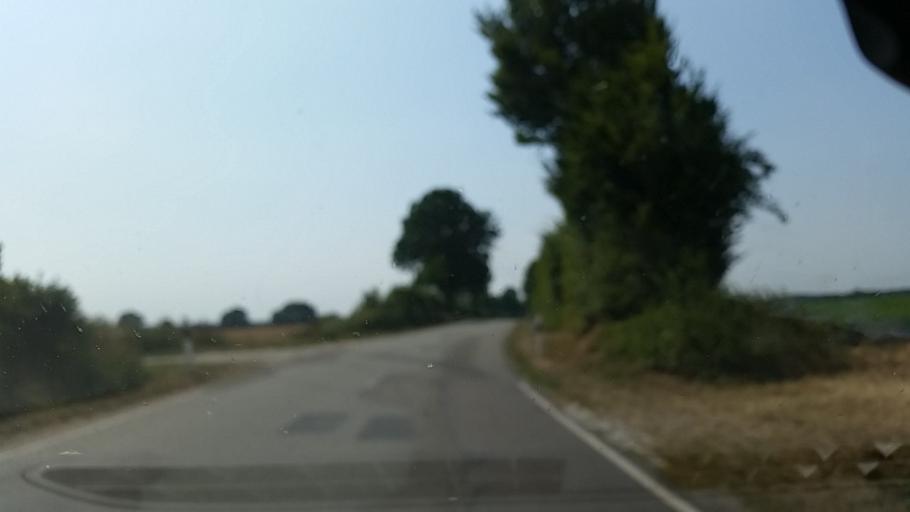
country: DE
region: Schleswig-Holstein
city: Walksfelde
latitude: 53.6381
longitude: 10.5893
